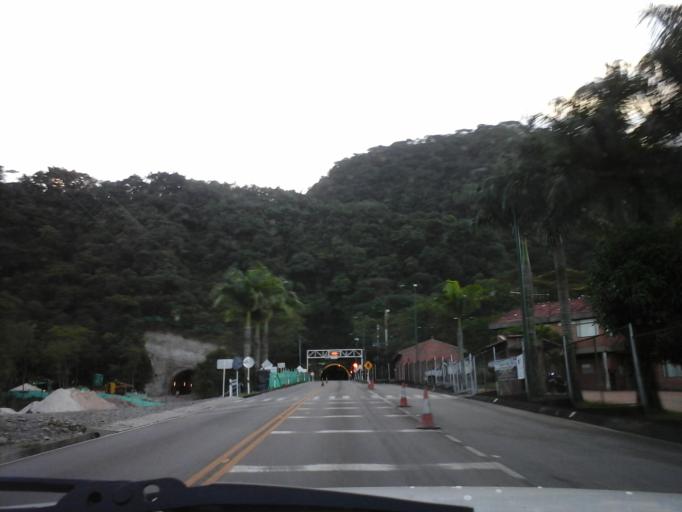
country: CO
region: Meta
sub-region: Villavicencio
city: Villavicencio
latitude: 4.1426
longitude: -73.6619
